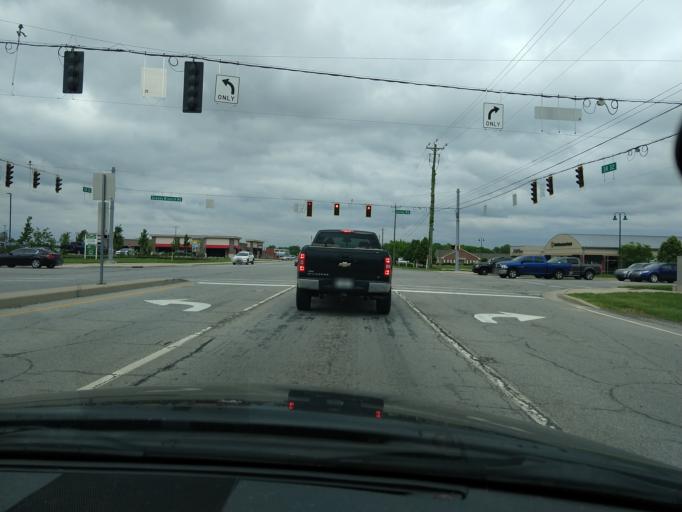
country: US
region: Indiana
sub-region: Hamilton County
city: Westfield
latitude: 40.0428
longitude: -86.1095
